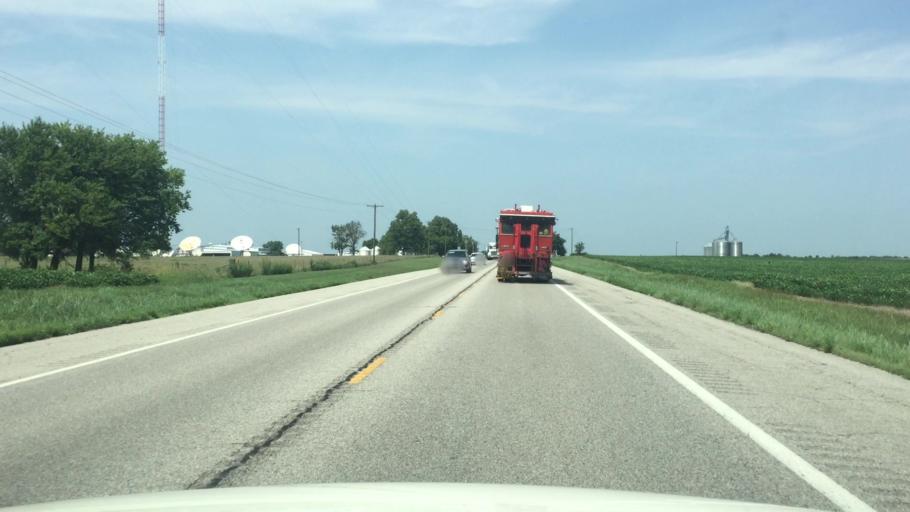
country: US
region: Missouri
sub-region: Jasper County
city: Carl Junction
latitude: 37.2178
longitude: -94.7048
